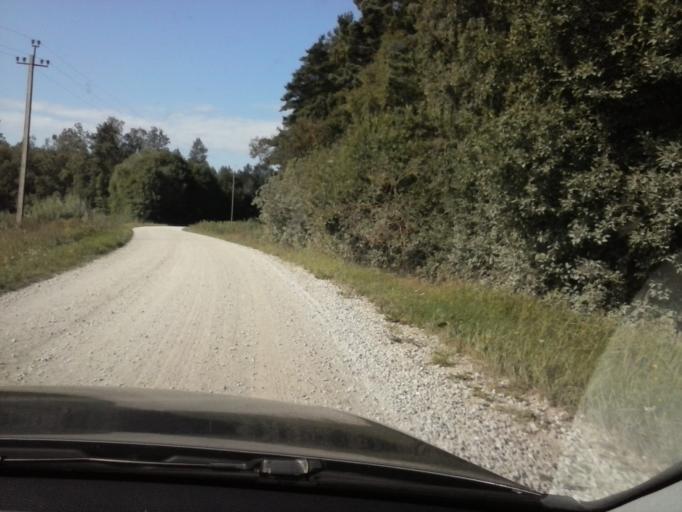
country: EE
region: Laeaene
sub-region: Haapsalu linn
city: Haapsalu
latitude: 58.8722
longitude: 23.5458
